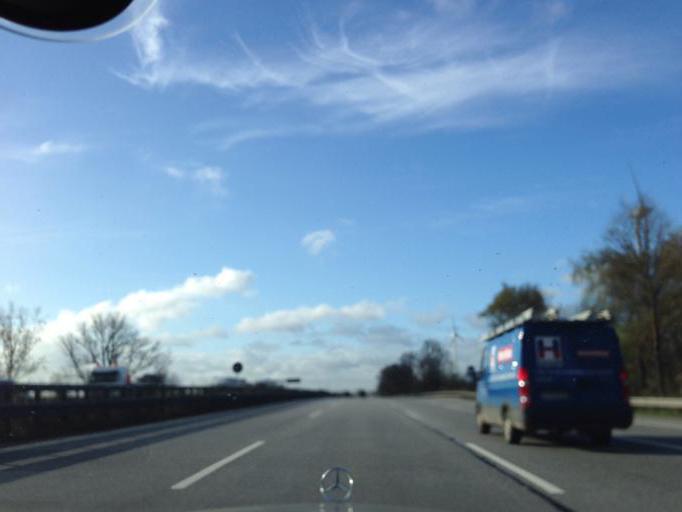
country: DE
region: Hamburg
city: Harburg
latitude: 53.4637
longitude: 10.0253
